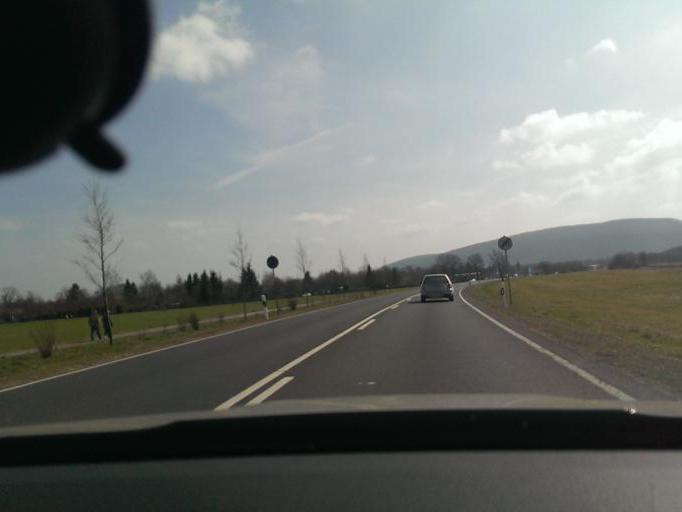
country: DE
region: Thuringia
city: Grafenhain
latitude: 50.8211
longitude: 10.7276
